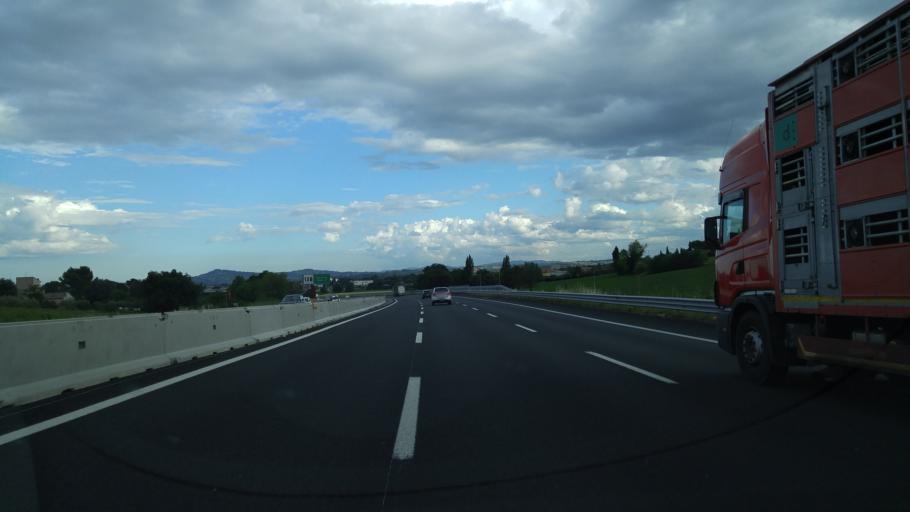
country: IT
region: Emilia-Romagna
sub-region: Provincia di Rimini
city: Riccione
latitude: 43.9733
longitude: 12.6641
